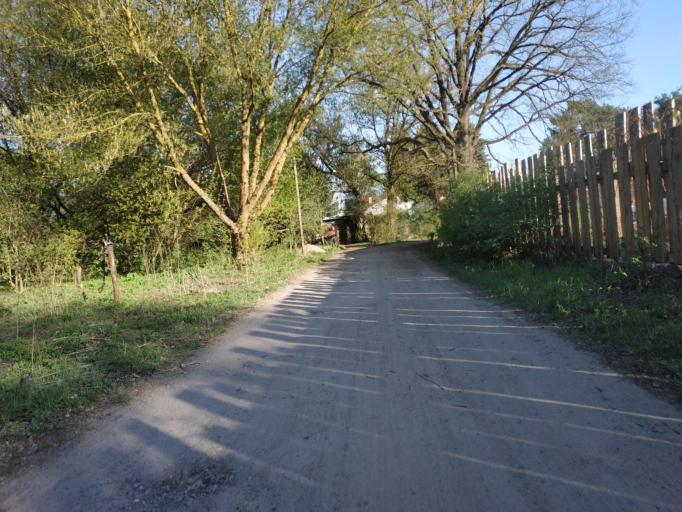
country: DE
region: Brandenburg
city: Strausberg
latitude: 52.5610
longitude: 13.8420
